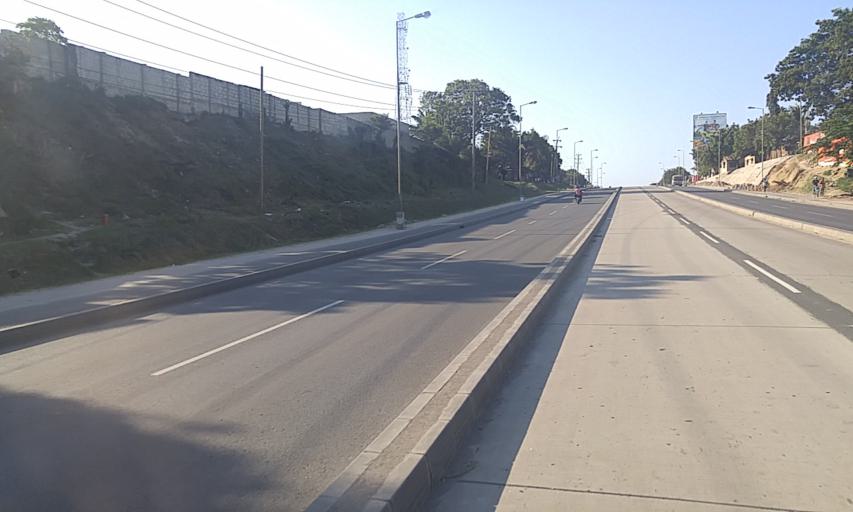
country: TZ
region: Dar es Salaam
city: Magomeni
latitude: -6.7995
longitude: 39.2628
